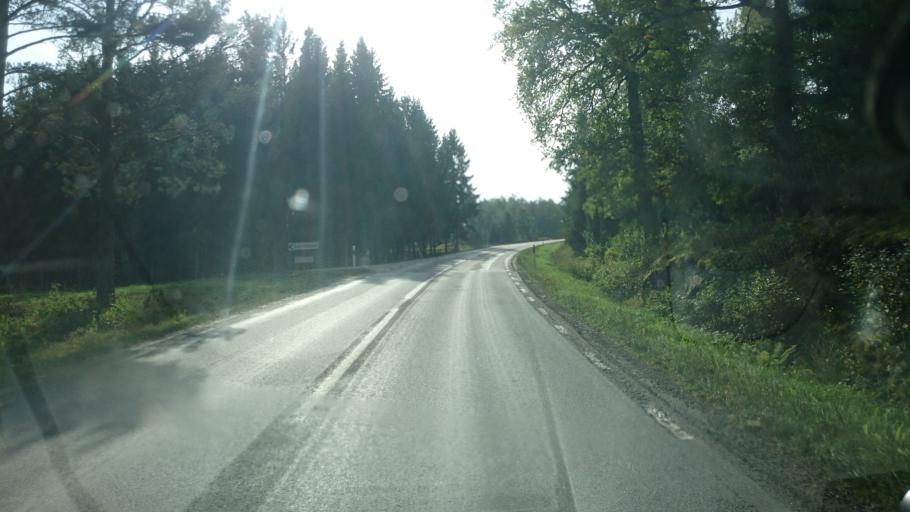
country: SE
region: Vaestra Goetaland
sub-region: Alingsas Kommun
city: Sollebrunn
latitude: 58.2138
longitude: 12.4324
